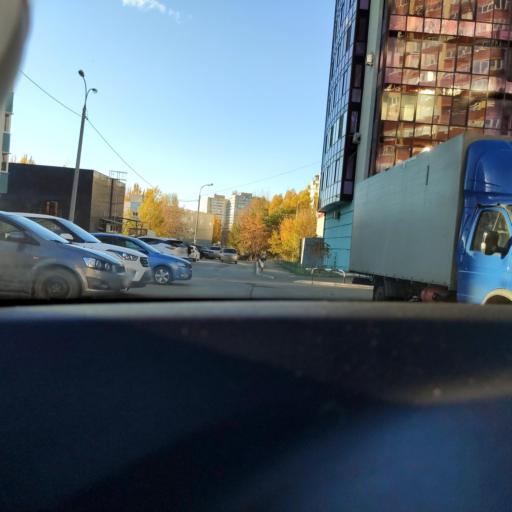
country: RU
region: Samara
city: Samara
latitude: 53.2582
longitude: 50.2195
